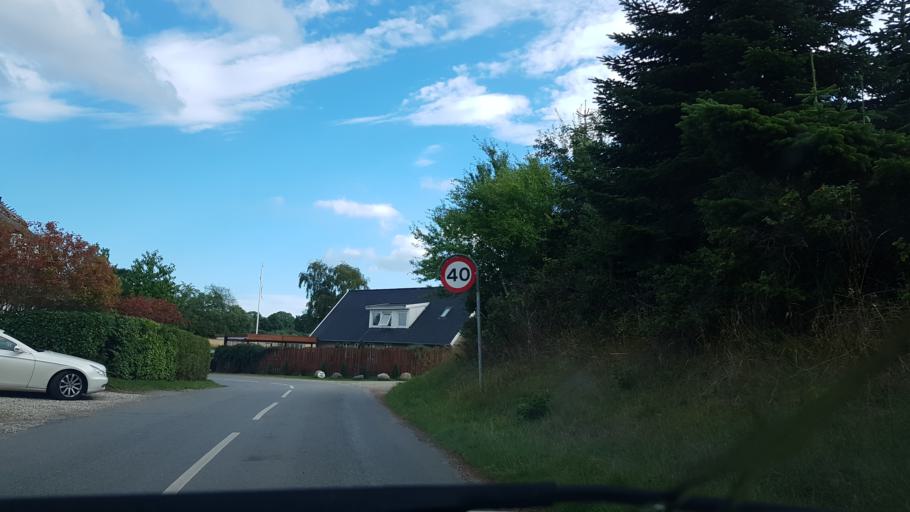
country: DK
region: Capital Region
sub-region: Fredensborg Kommune
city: Niva
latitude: 55.9522
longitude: 12.5068
